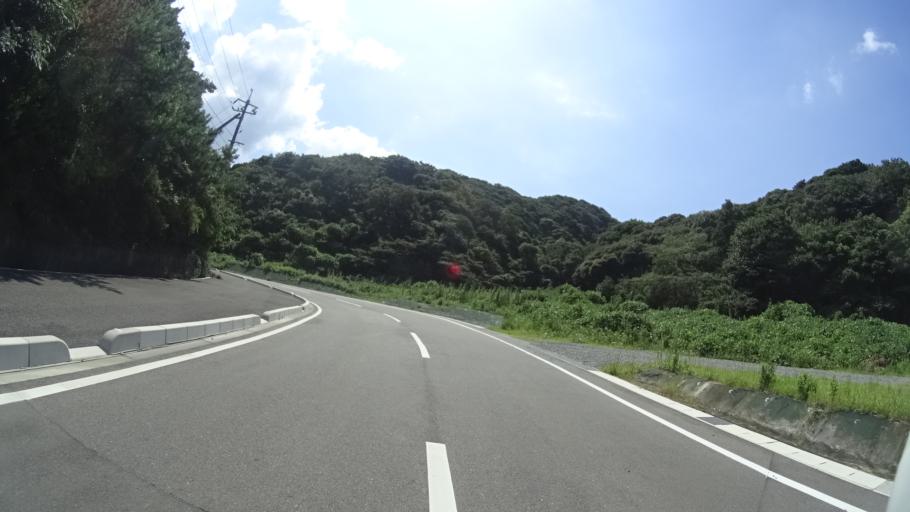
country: JP
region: Yamaguchi
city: Shimonoseki
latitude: 34.0969
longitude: 130.8759
